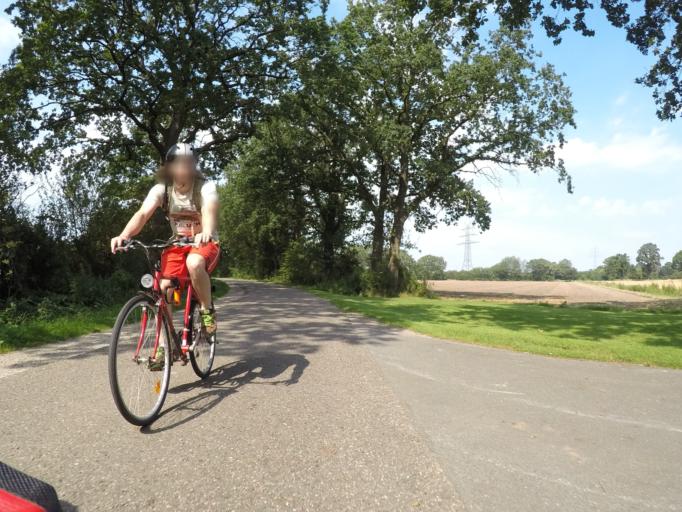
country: DE
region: Schleswig-Holstein
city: Kisdorf
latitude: 53.7791
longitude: 10.0281
